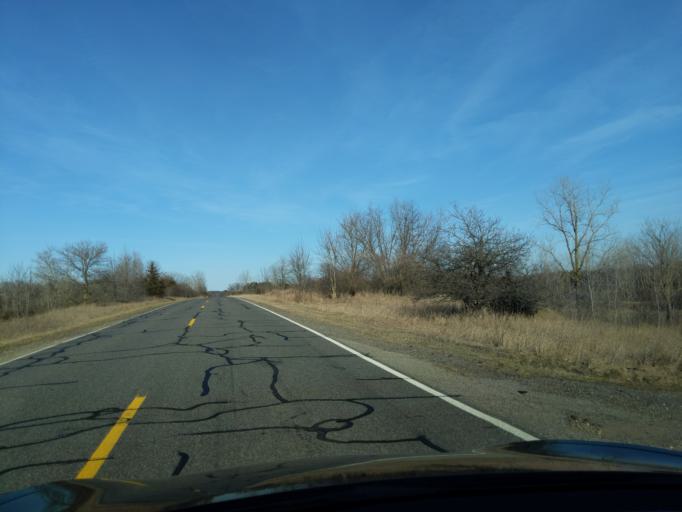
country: US
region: Michigan
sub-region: Ionia County
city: Saranac
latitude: 42.9493
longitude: -85.1609
